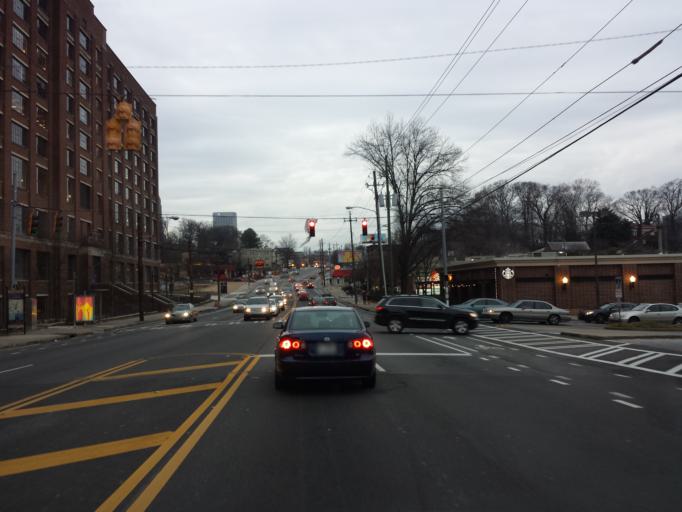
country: US
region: Georgia
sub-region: DeKalb County
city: Druid Hills
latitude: 33.7734
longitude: -84.3653
